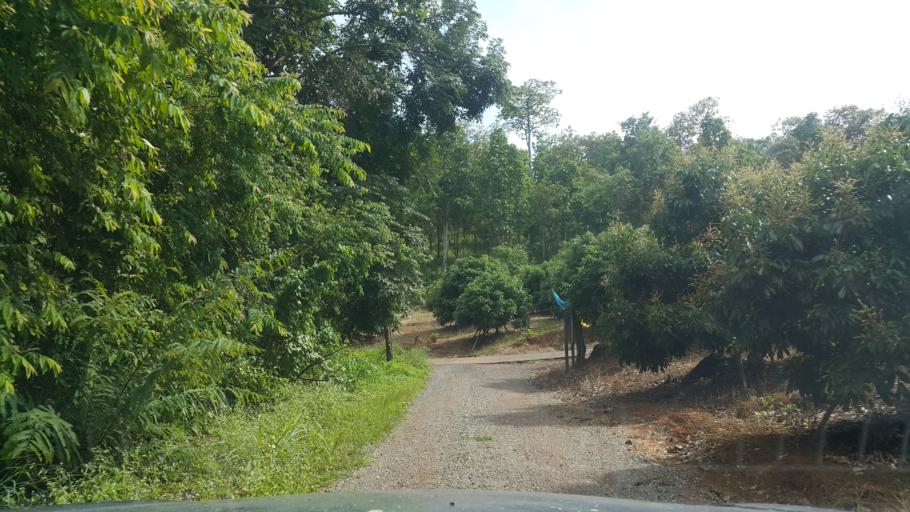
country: TH
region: Chiang Mai
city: Mae Taeng
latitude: 19.2288
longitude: 99.0070
